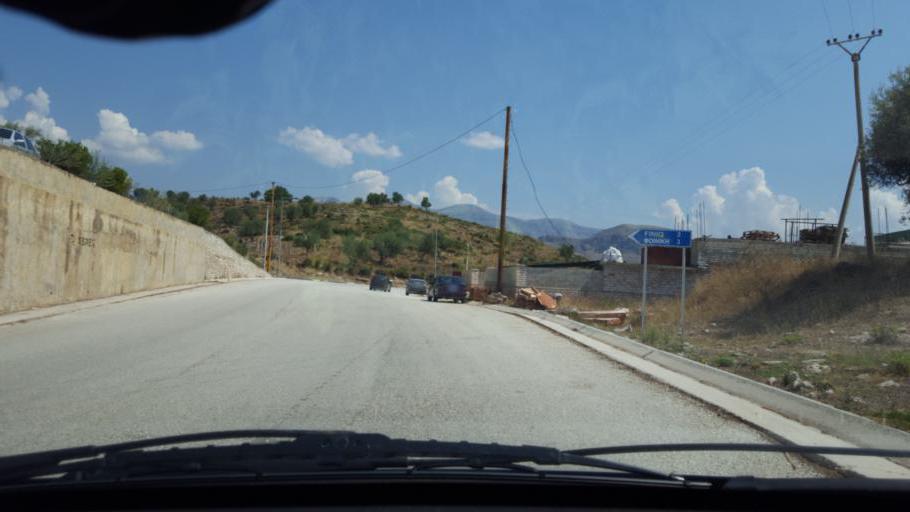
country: AL
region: Vlore
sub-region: Rrethi i Delvines
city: Mesopotam
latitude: 39.8991
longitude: 20.0771
